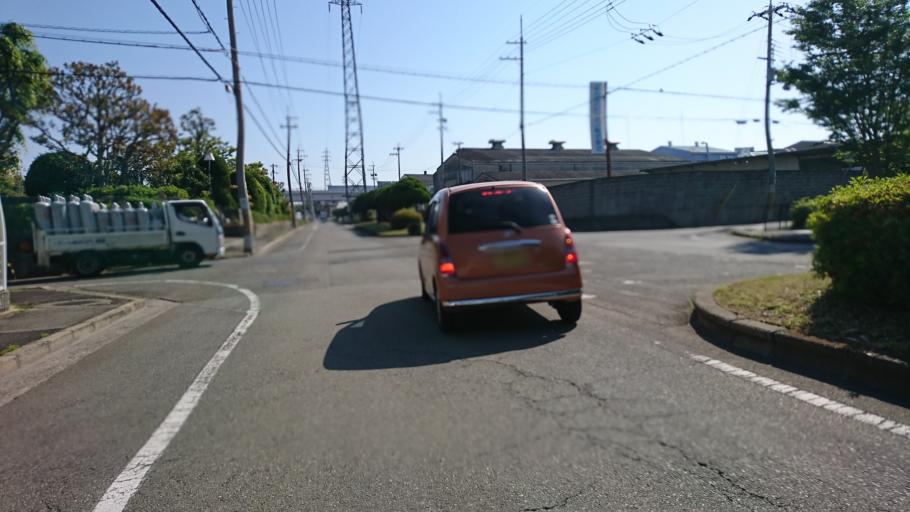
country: JP
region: Hyogo
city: Kakogawacho-honmachi
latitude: 34.7625
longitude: 134.8675
